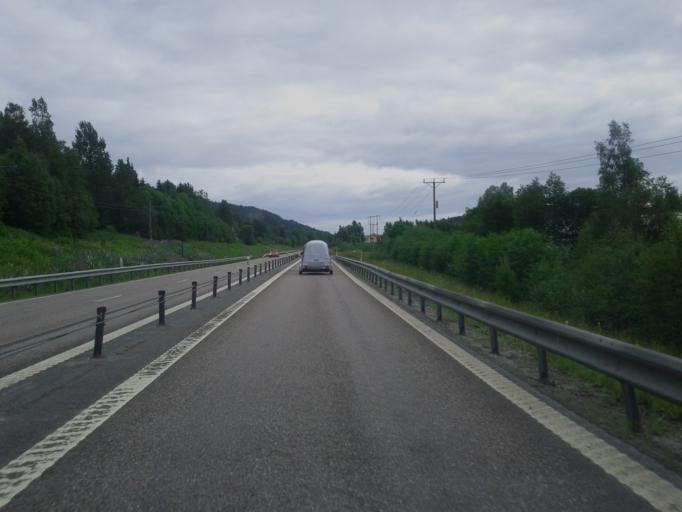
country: SE
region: Vaesternorrland
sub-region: OErnskoeldsviks Kommun
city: Ornskoldsvik
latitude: 63.2979
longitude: 18.6473
